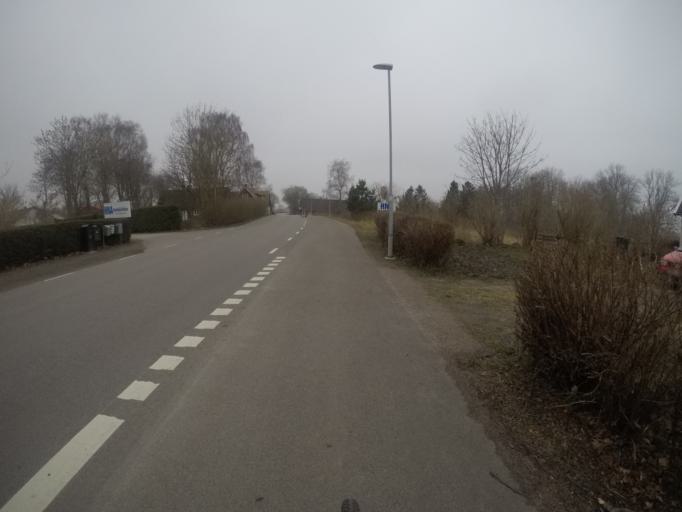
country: SE
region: Skane
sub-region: Angelholms Kommun
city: Strovelstorp
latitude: 56.2218
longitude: 12.7549
